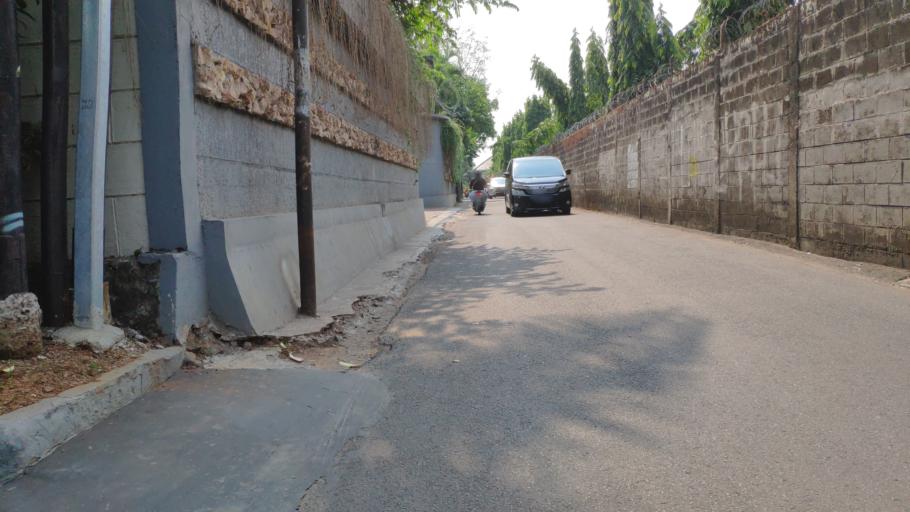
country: ID
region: Jakarta Raya
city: Jakarta
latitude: -6.2658
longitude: 106.8229
